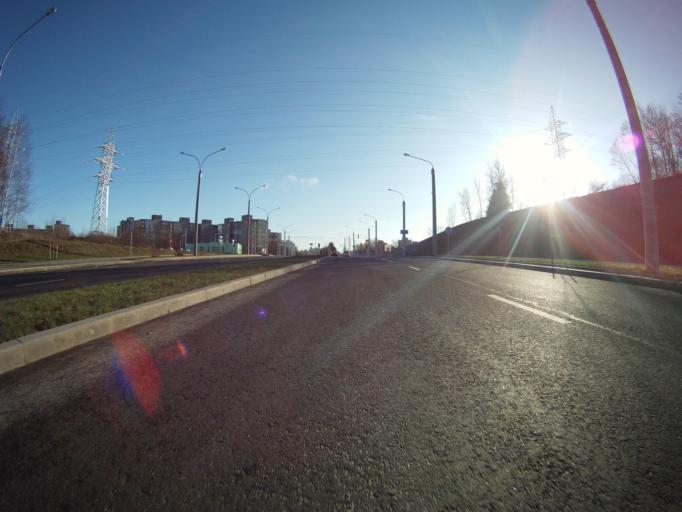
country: BY
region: Minsk
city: Novoye Medvezhino
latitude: 53.8711
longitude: 27.4585
